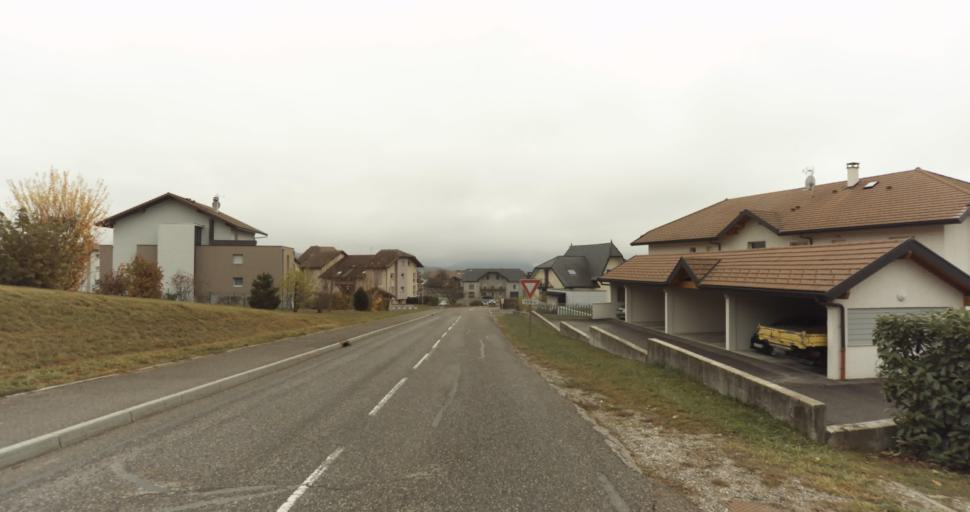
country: FR
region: Rhone-Alpes
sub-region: Departement de la Haute-Savoie
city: Groisy
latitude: 46.0110
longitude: 6.1702
